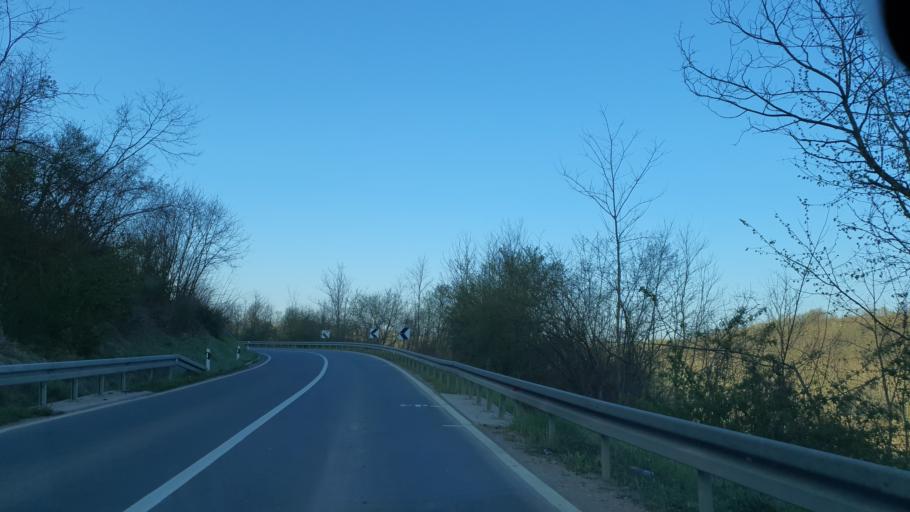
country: RS
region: Central Serbia
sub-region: Kolubarski Okrug
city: Osecina
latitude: 44.4187
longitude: 19.5387
